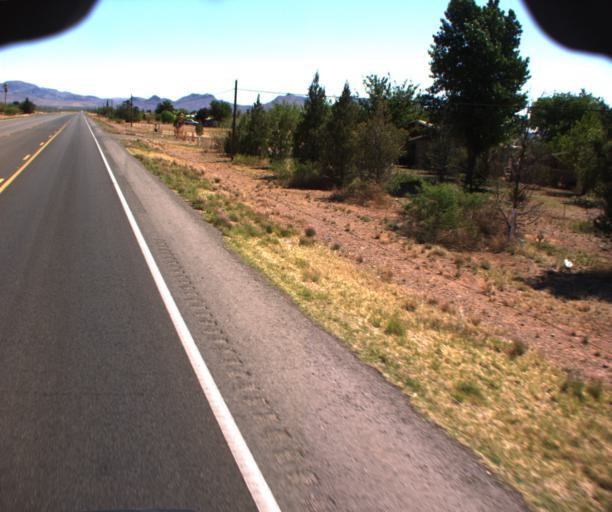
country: US
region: Arizona
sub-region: Cochise County
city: Douglas
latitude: 31.3658
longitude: -109.5387
